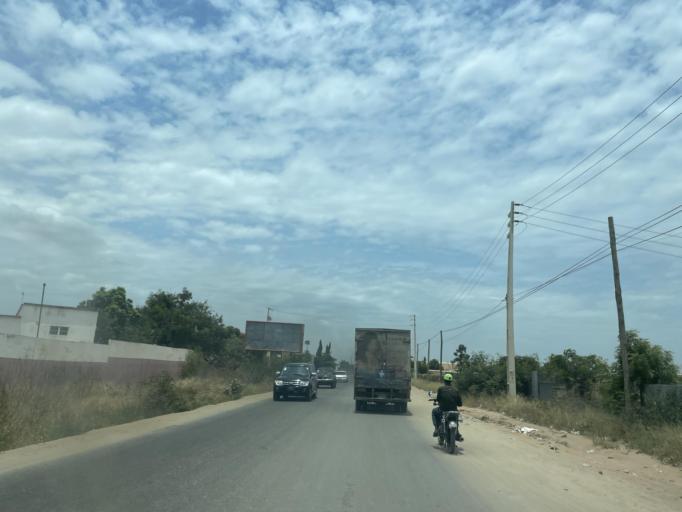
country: AO
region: Luanda
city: Luanda
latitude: -8.9445
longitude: 13.3851
